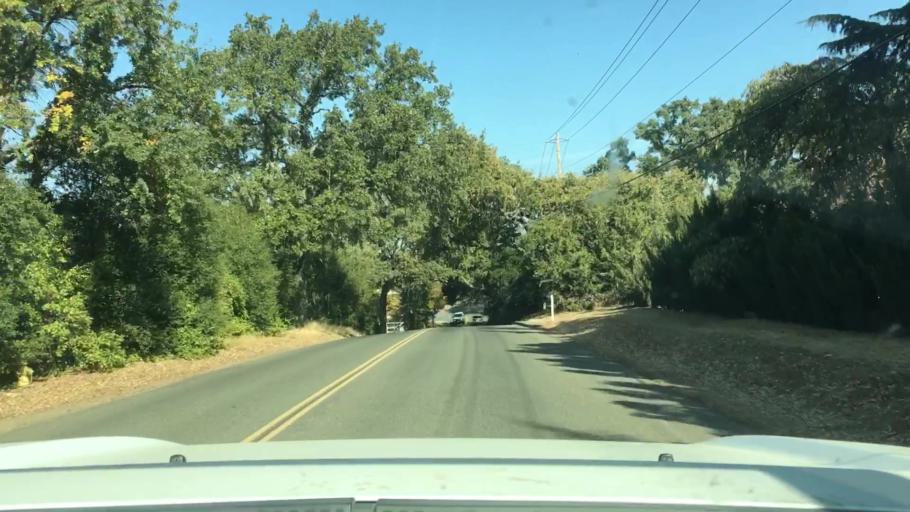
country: US
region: California
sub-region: San Luis Obispo County
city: Templeton
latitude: 35.5464
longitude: -120.7300
